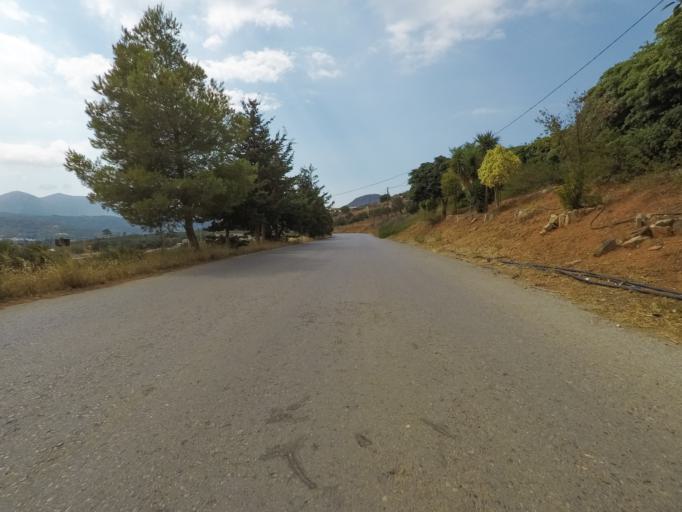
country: GR
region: Crete
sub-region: Nomos Lasithiou
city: Neapoli
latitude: 35.2612
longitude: 25.6103
